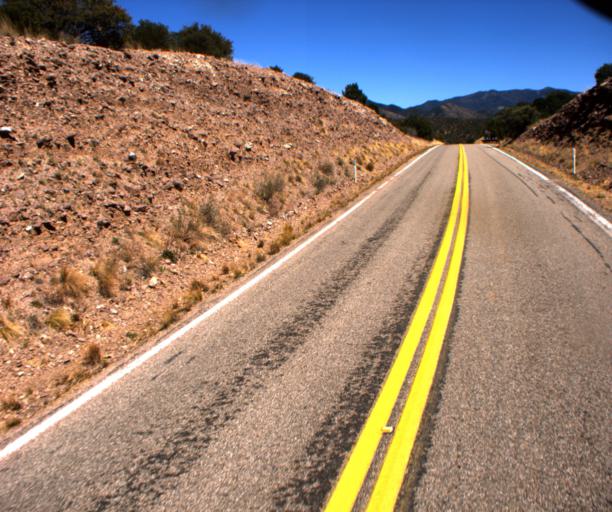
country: US
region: Arizona
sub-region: Cochise County
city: Sierra Vista
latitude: 31.4713
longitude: -110.4701
